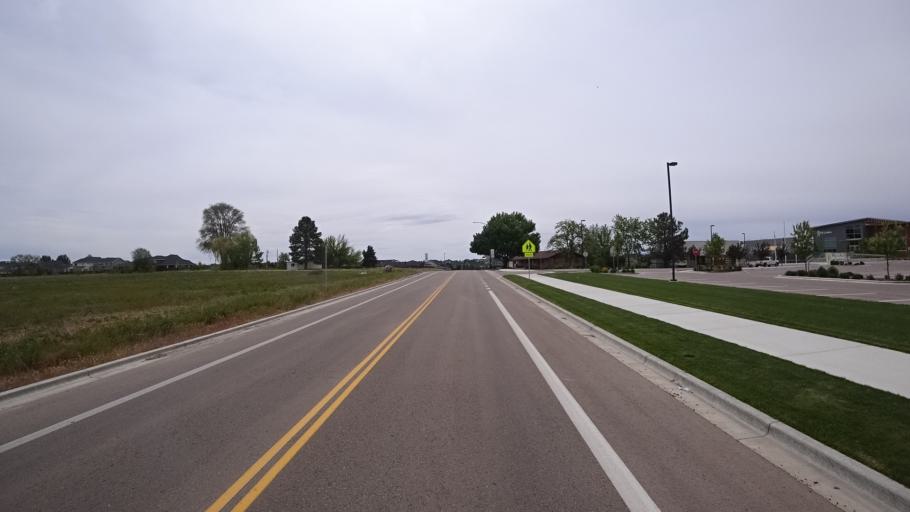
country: US
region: Idaho
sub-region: Ada County
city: Meridian
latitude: 43.5587
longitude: -116.3444
